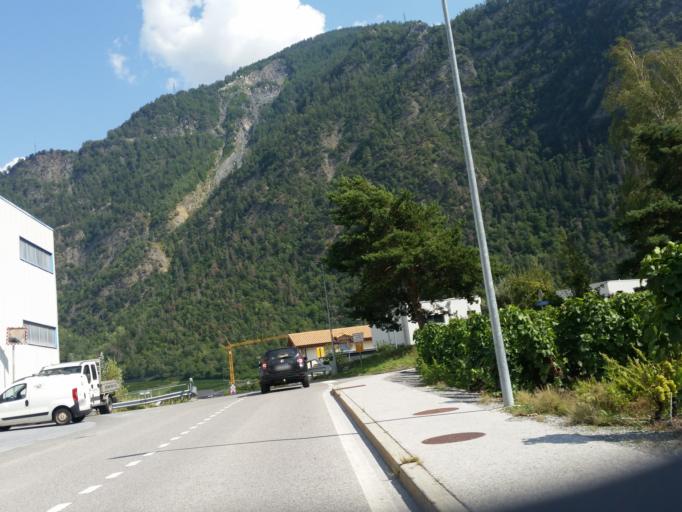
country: CH
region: Valais
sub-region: Martigny District
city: Riddes
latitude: 46.1756
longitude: 7.2273
